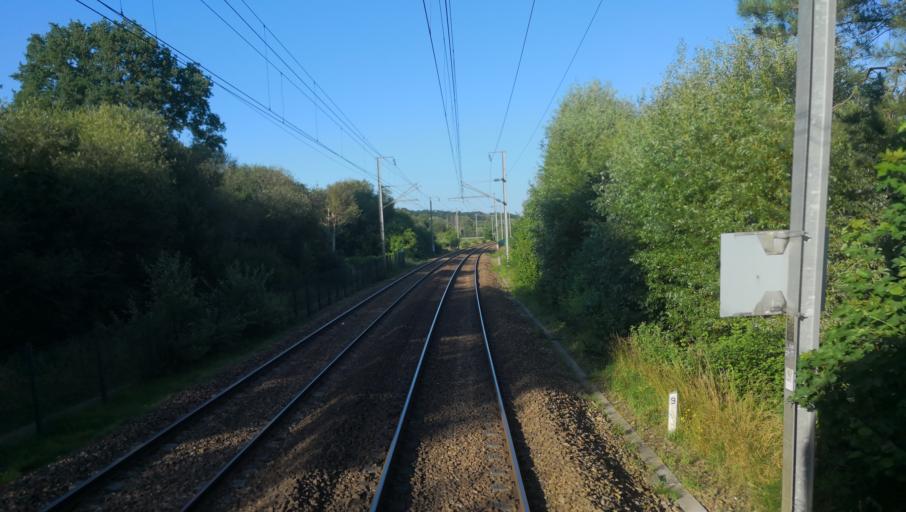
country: FR
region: Haute-Normandie
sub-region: Departement de l'Eure
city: Saint-Sebastien-de-Morsent
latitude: 48.9934
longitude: 1.0473
